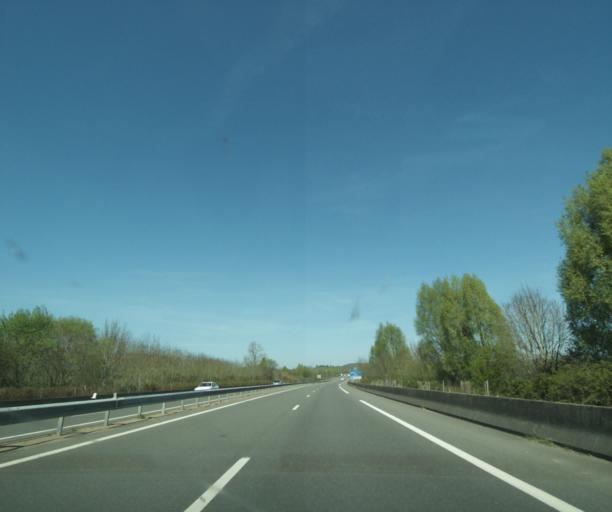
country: FR
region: Bourgogne
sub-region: Departement de la Nievre
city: Pougues-les-Eaux
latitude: 47.0658
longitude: 3.1291
